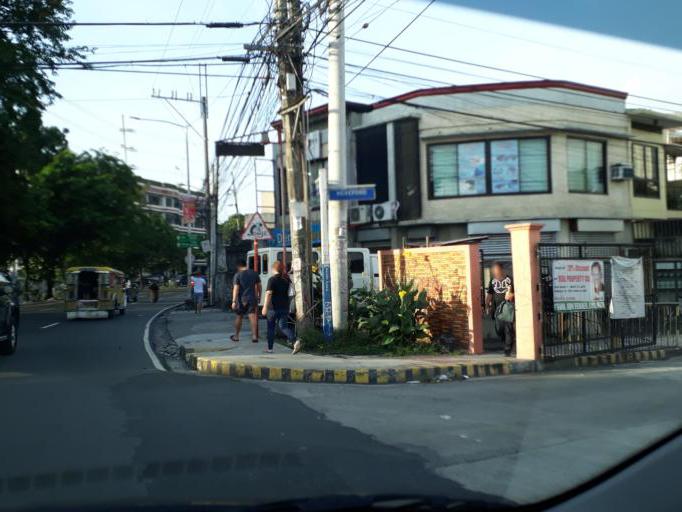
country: PH
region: Calabarzon
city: Bagong Pagasa
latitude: 14.6618
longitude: 121.0203
